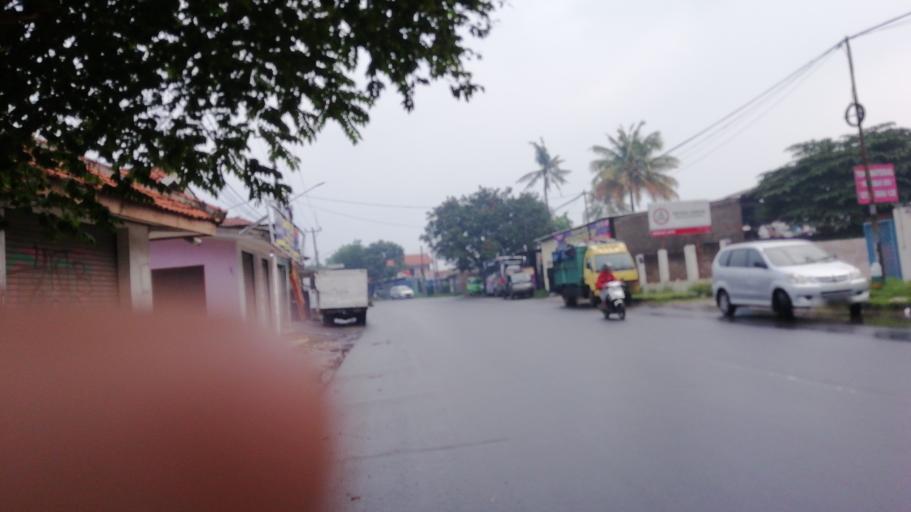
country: ID
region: West Java
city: Bogor
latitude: -6.5401
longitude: 106.8060
